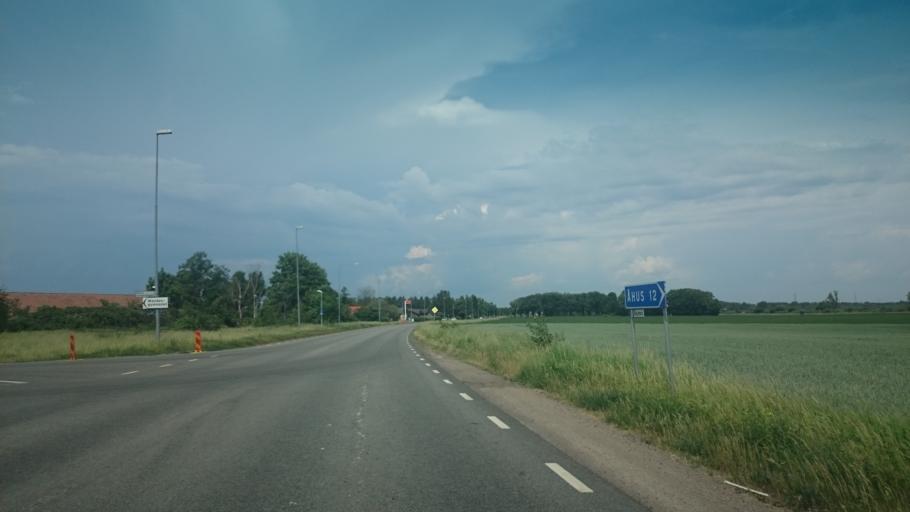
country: SE
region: Skane
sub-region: Kristianstads Kommun
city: Norra Asum
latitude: 55.9965
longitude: 14.1515
